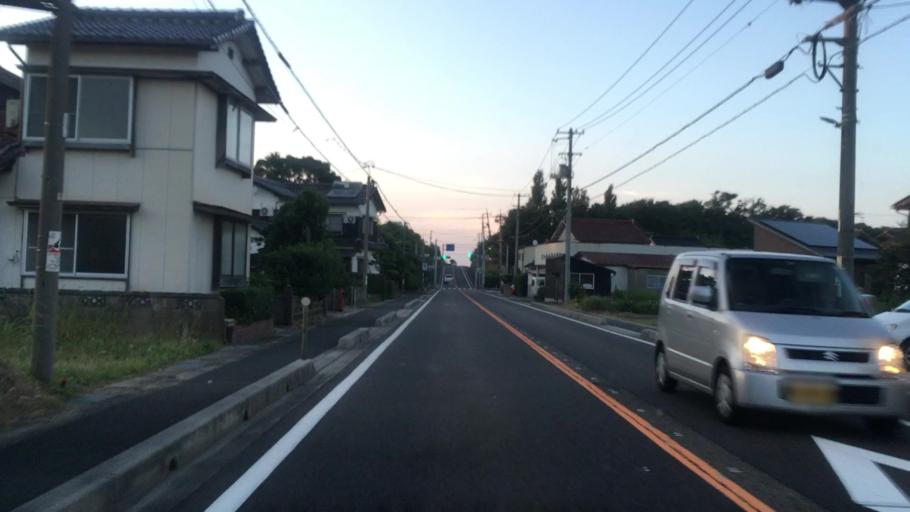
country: JP
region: Tottori
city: Tottori
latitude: 35.5854
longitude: 134.3326
